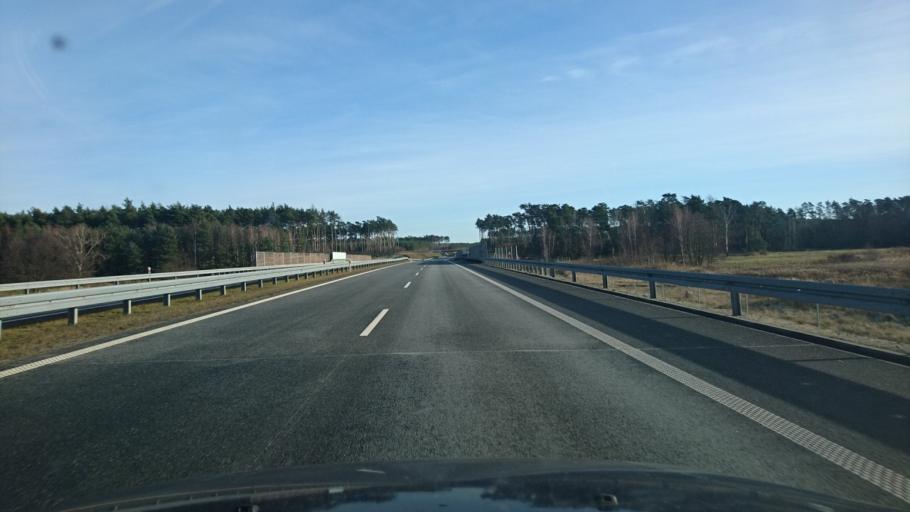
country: PL
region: Greater Poland Voivodeship
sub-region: Powiat kepinski
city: Kepno
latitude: 51.3308
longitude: 17.9642
